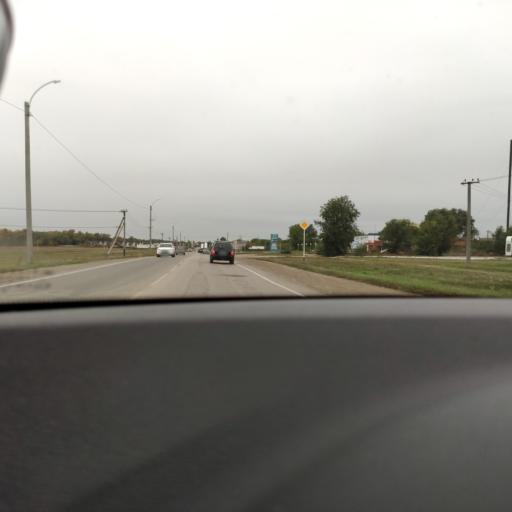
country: RU
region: Samara
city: Krasnyy Yar
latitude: 53.4817
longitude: 50.3920
